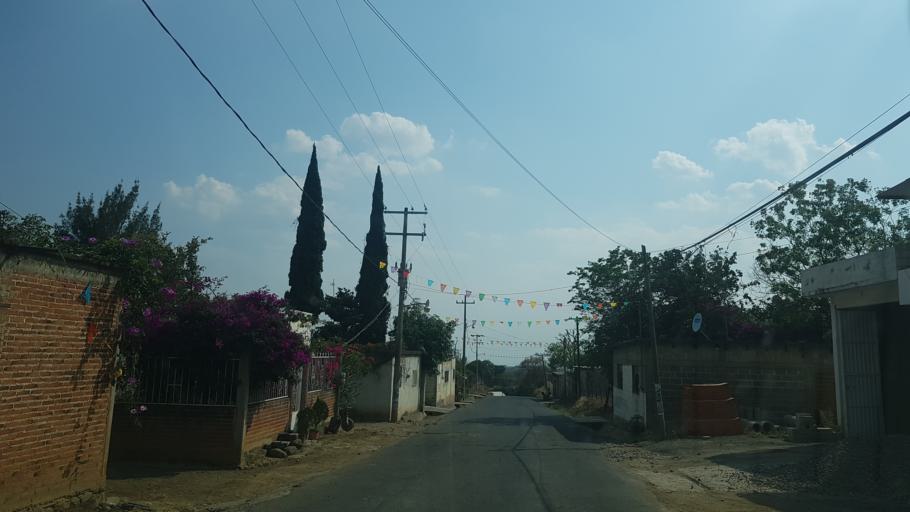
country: MX
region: Puebla
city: San Juan Amecac
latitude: 18.8319
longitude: -98.7040
